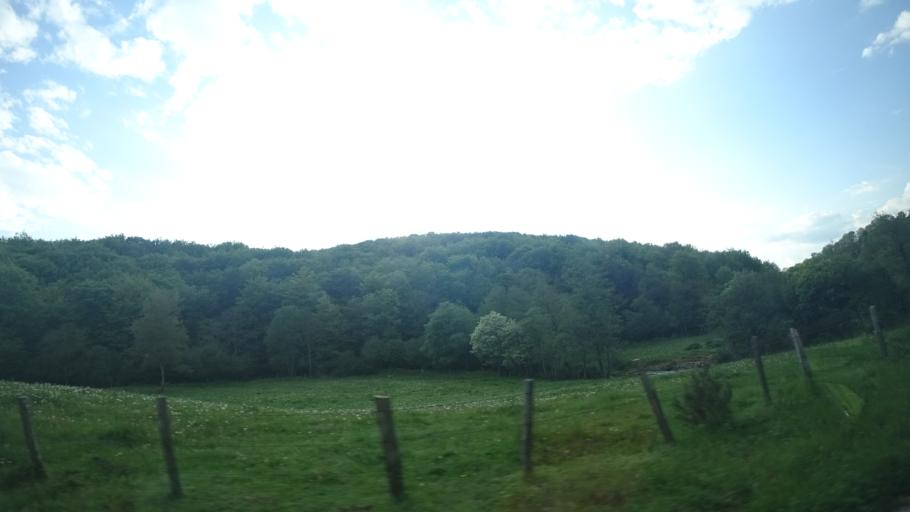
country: FR
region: Midi-Pyrenees
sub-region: Departement de l'Aveyron
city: Severac-le-Chateau
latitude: 44.2575
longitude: 2.9224
